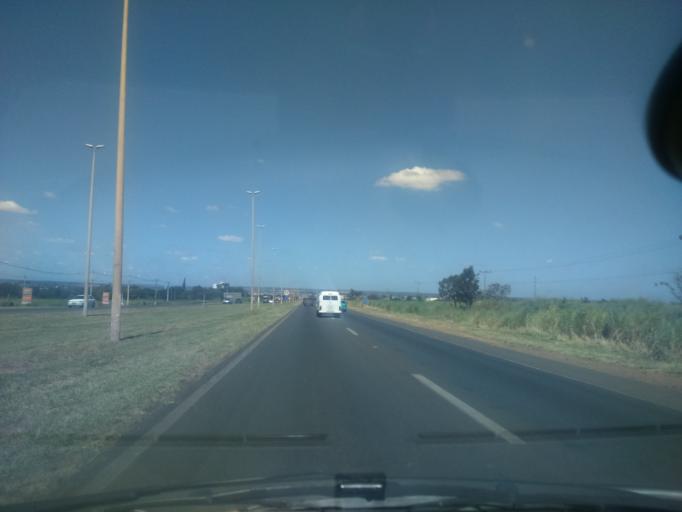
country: BR
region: Goias
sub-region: Luziania
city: Luziania
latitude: -16.0998
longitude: -47.9780
